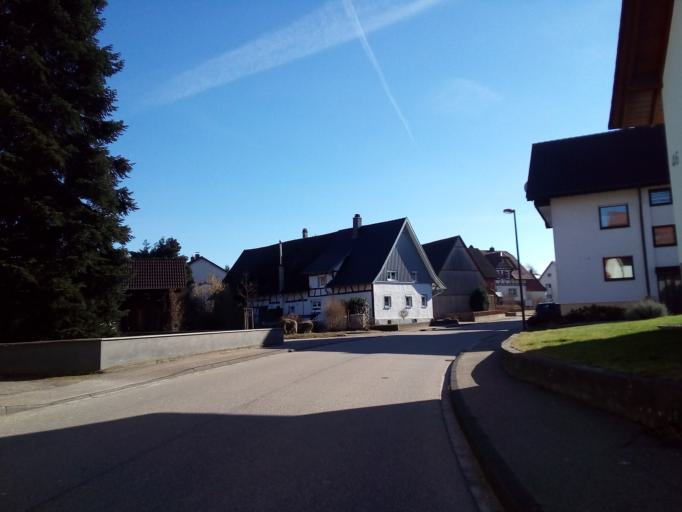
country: DE
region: Baden-Wuerttemberg
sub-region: Freiburg Region
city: Renchen
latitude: 48.6033
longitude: 8.0388
